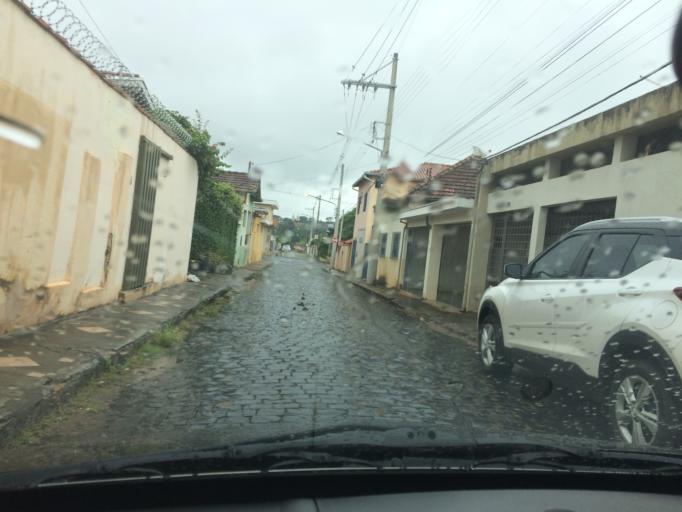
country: BR
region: Sao Paulo
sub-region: Casa Branca
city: Casa Branca
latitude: -21.7719
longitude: -47.0888
